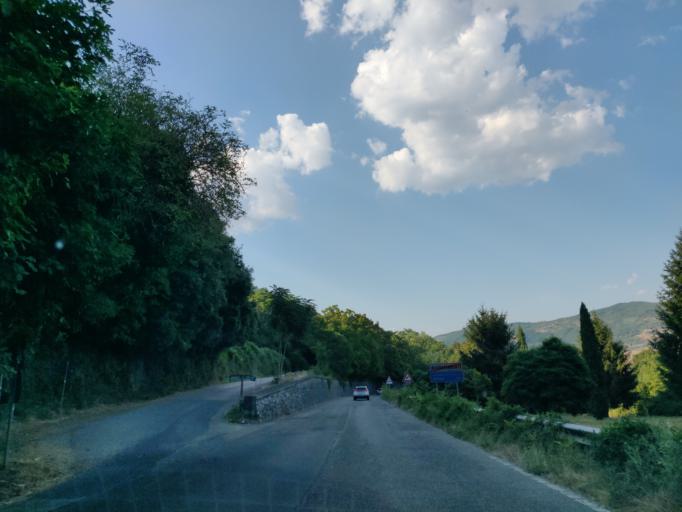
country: IT
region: Latium
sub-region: Provincia di Viterbo
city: Acquapendente
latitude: 42.7505
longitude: 11.8625
